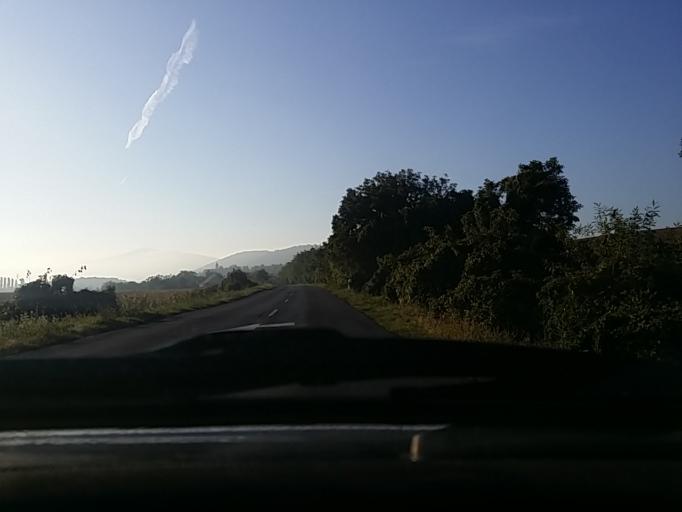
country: HU
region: Komarom-Esztergom
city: Pilismarot
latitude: 47.7937
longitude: 18.8651
